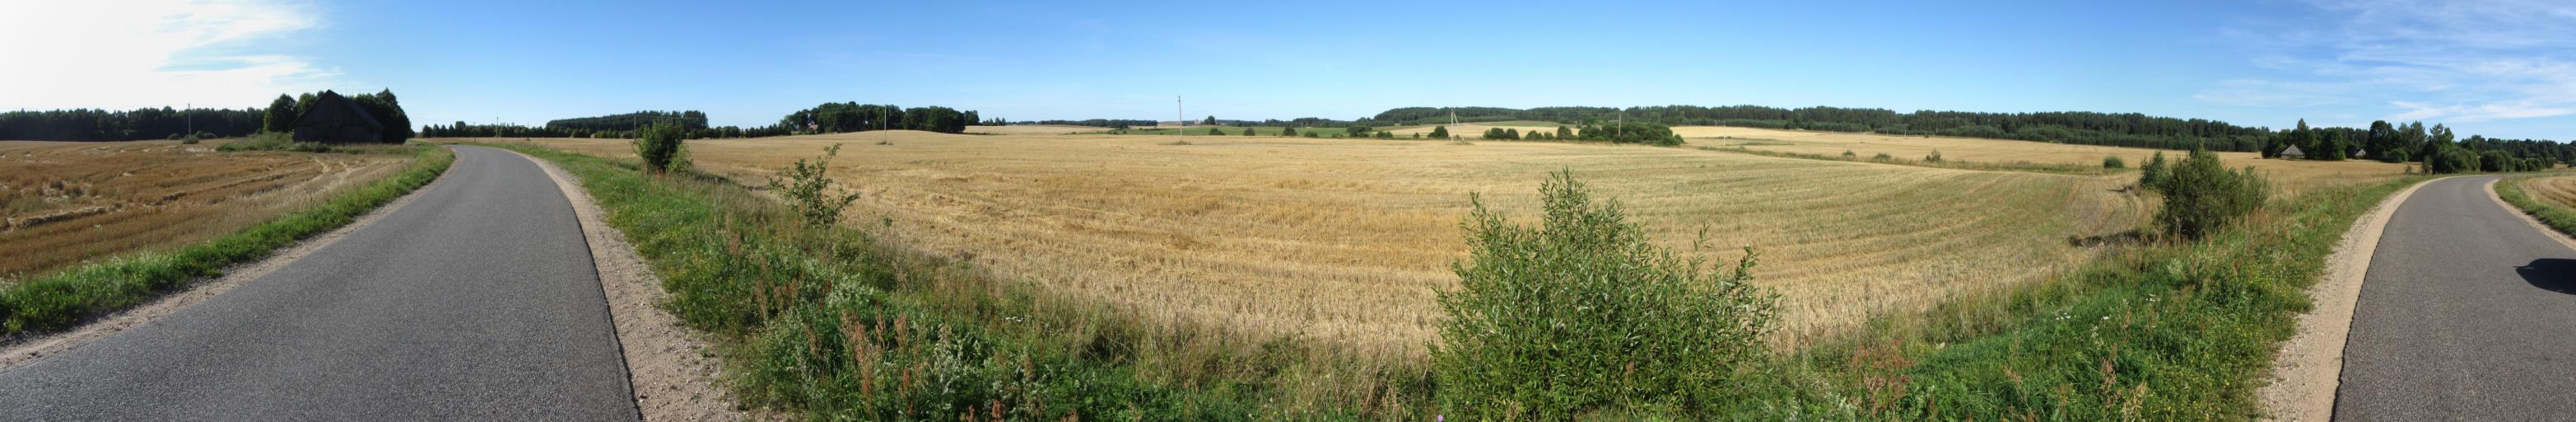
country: LT
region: Panevezys
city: Rokiskis
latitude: 55.7309
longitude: 25.4245
